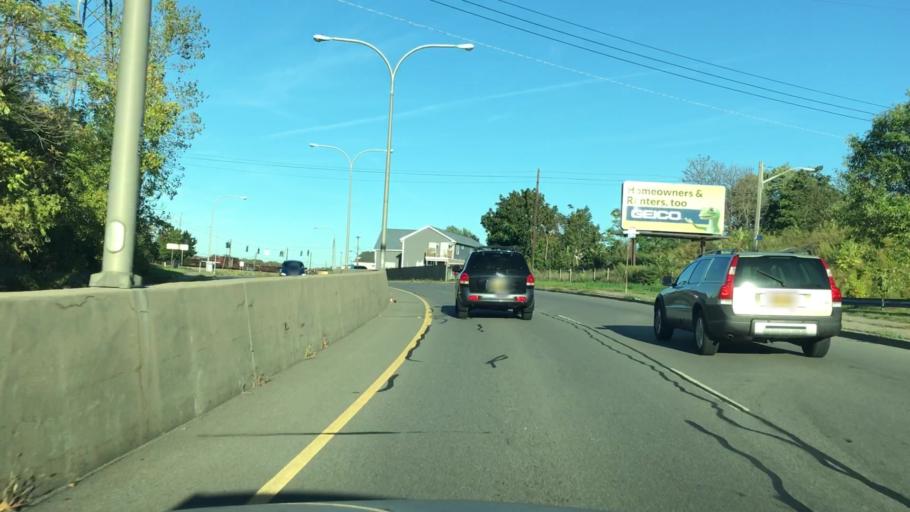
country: US
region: New York
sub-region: Erie County
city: Sloan
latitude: 42.8975
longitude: -78.8043
